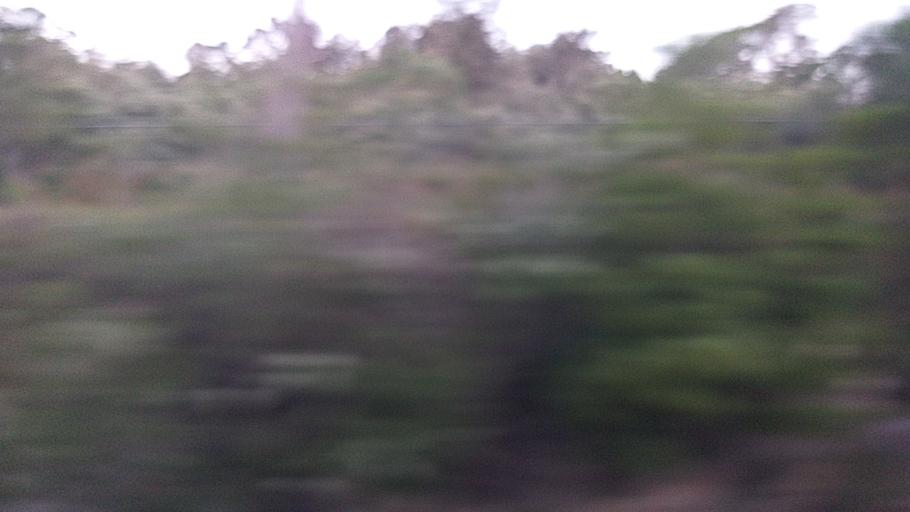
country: AU
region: New South Wales
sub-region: Sutherland Shire
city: Heathcote
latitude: -34.0786
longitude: 151.0117
